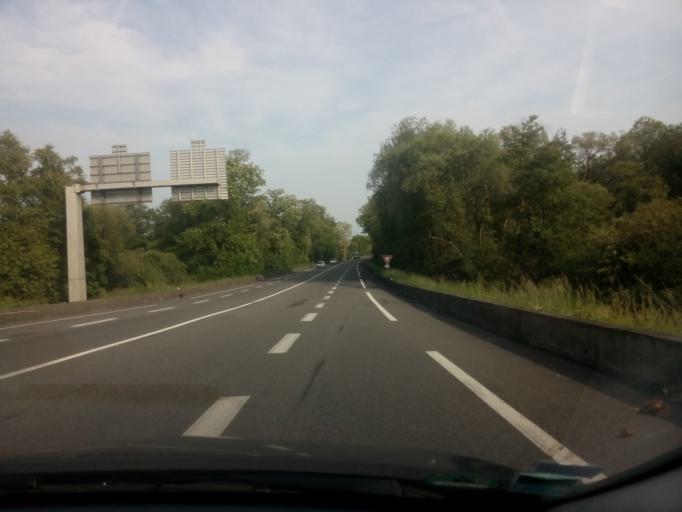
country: FR
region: Alsace
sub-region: Departement du Bas-Rhin
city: Roppenheim
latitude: 48.8540
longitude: 8.0568
